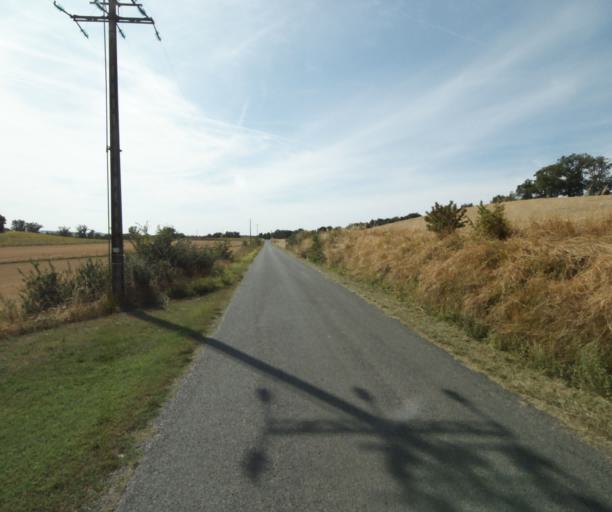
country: FR
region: Midi-Pyrenees
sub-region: Departement du Tarn
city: Puylaurens
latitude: 43.5247
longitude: 2.0548
